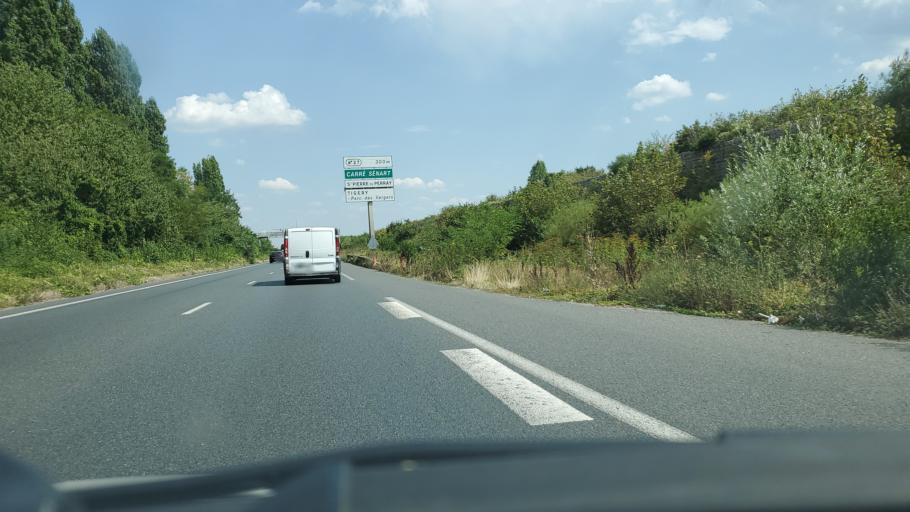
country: FR
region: Ile-de-France
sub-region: Departement de l'Essonne
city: Tigery
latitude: 48.6314
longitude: 2.5043
